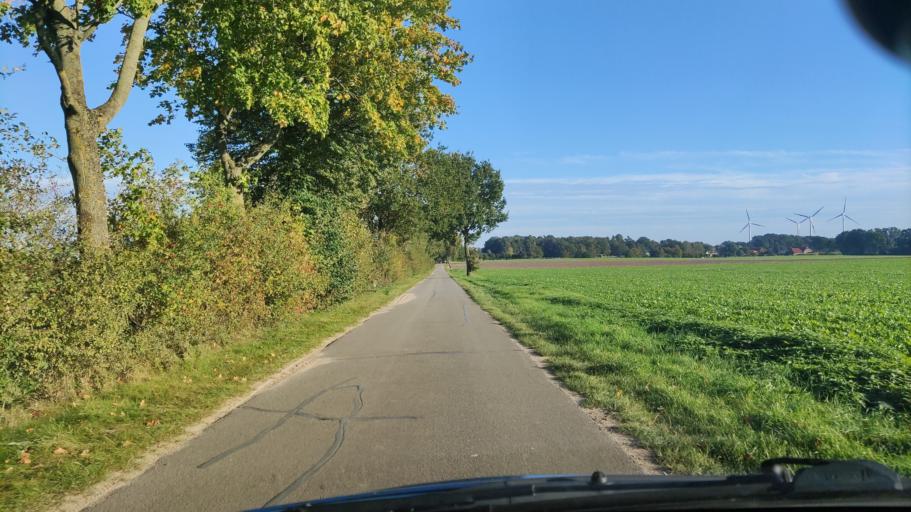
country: DE
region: Lower Saxony
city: Sudergellersen
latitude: 53.2136
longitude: 10.2832
